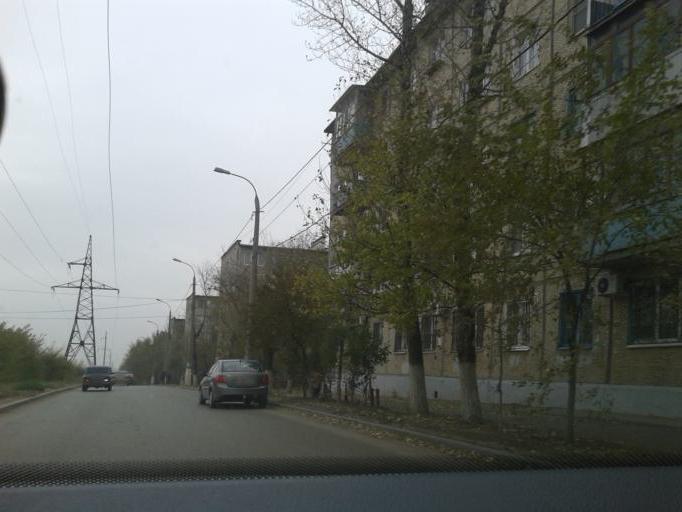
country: RU
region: Volgograd
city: Gorodishche
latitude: 48.7671
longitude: 44.4795
